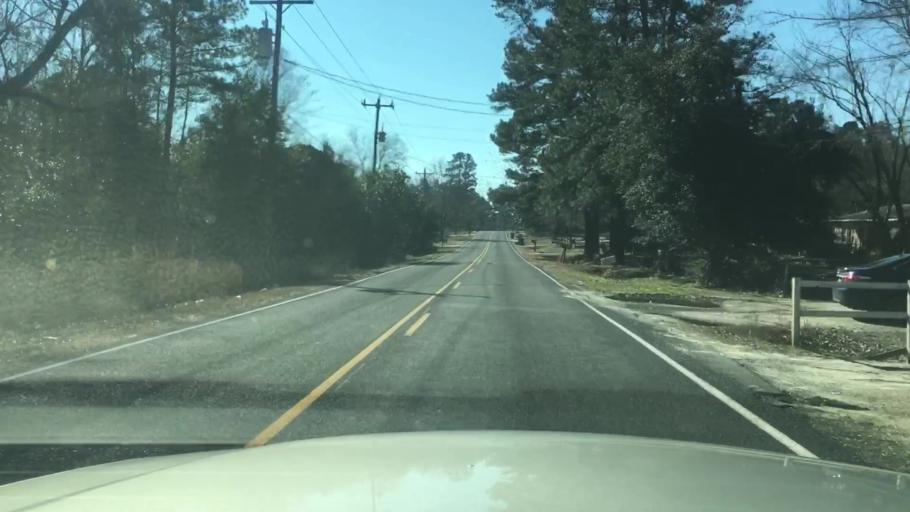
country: US
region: North Carolina
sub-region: Cumberland County
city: Hope Mills
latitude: 35.0006
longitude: -78.9647
